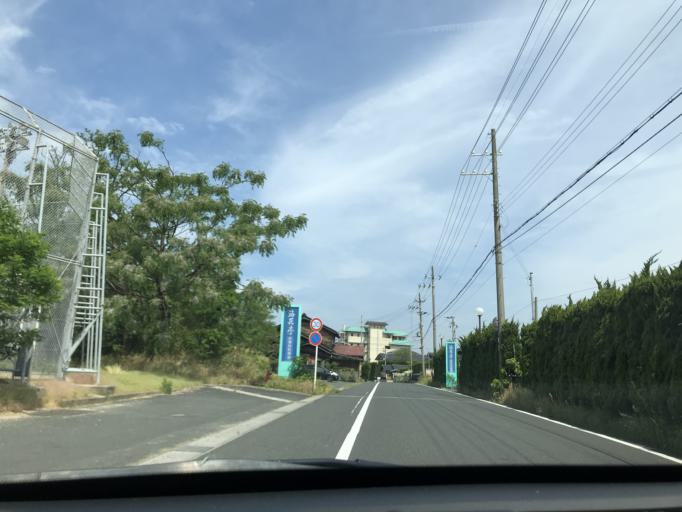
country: JP
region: Hyogo
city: Toyooka
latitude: 35.6578
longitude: 134.9660
